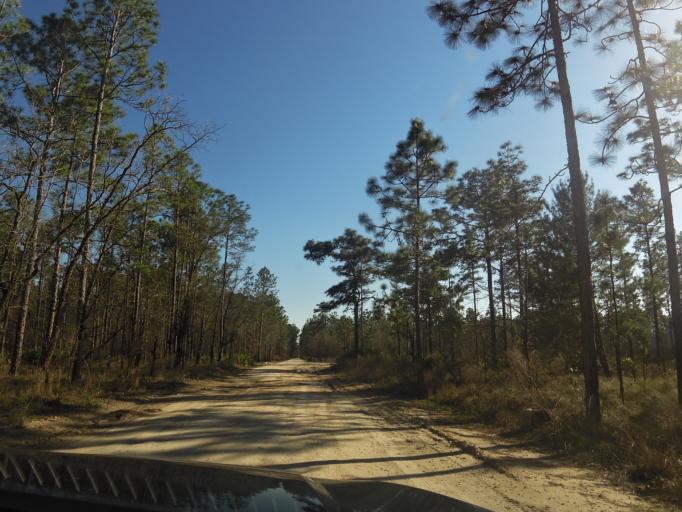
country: US
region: Florida
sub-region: Clay County
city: Middleburg
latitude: 30.1527
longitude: -81.8822
